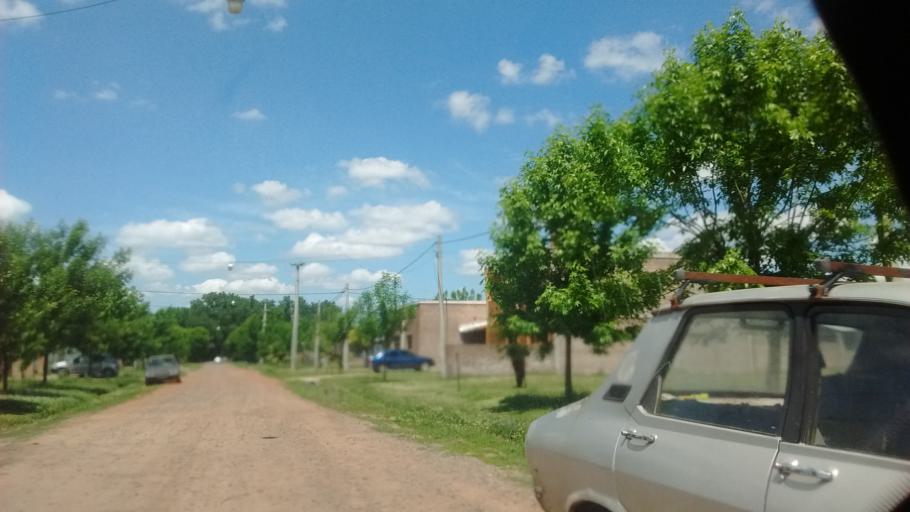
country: AR
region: Santa Fe
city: Funes
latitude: -32.8510
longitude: -60.7969
